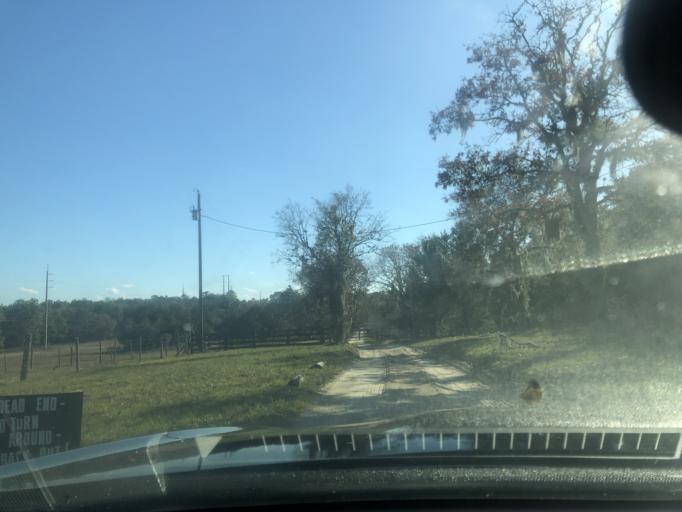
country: US
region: Florida
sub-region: Citrus County
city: Lecanto
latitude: 28.8172
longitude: -82.5181
